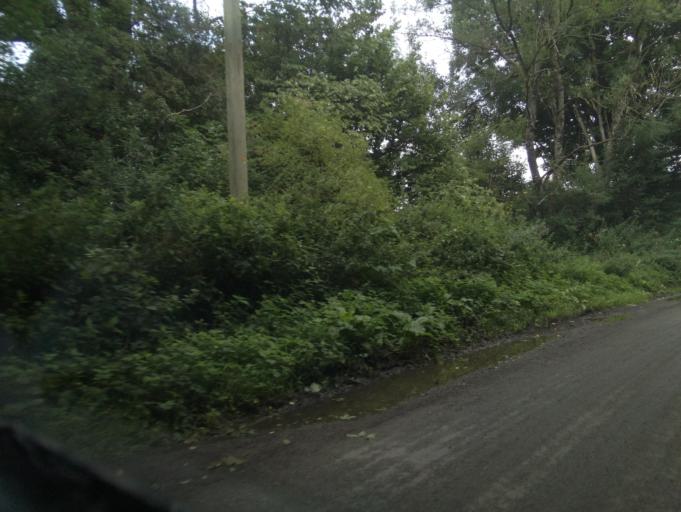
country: GB
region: England
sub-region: Somerset
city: Evercreech
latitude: 51.1799
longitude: -2.5073
